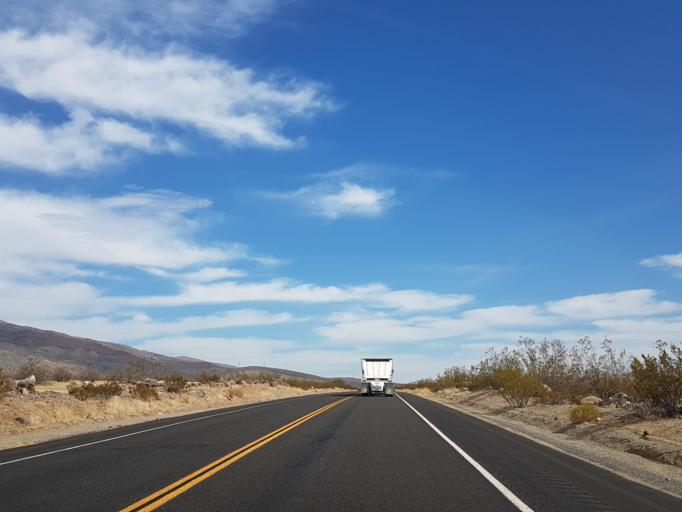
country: US
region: California
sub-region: Kern County
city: Ridgecrest
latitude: 35.4208
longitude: -117.7406
